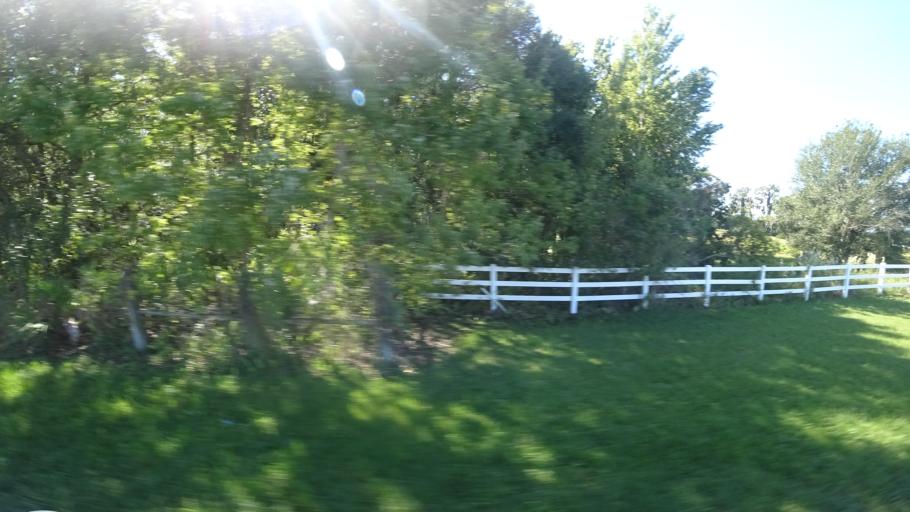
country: US
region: Florida
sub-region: Sarasota County
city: Lake Sarasota
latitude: 27.3499
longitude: -82.2589
